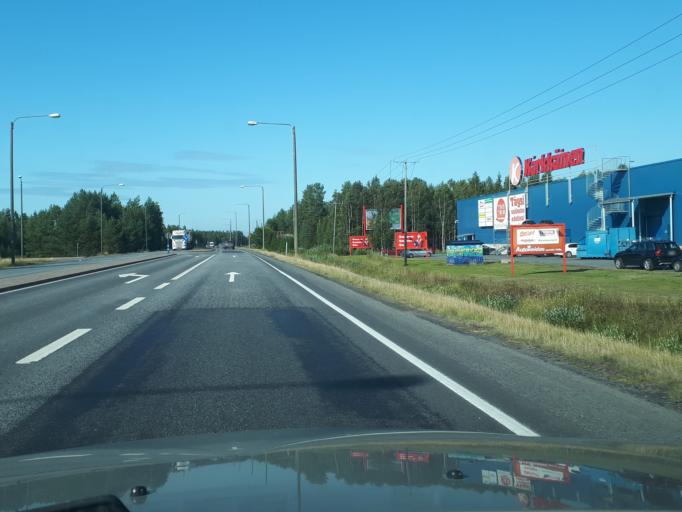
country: FI
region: Northern Ostrobothnia
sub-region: Oulunkaari
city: Ii
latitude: 65.2905
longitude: 25.3732
